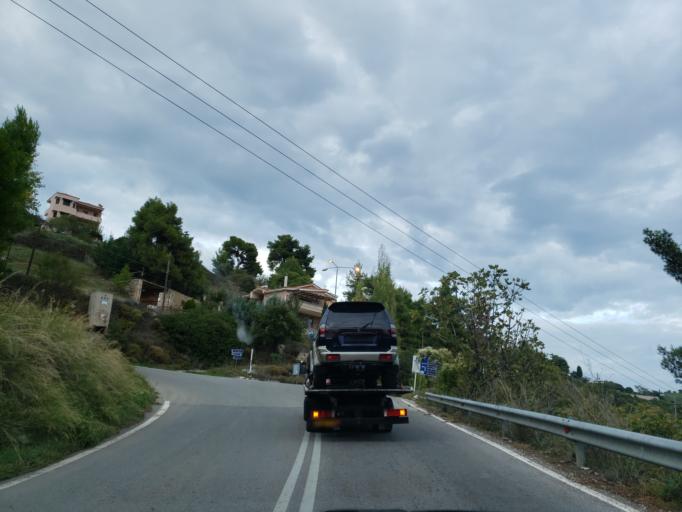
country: GR
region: Attica
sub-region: Nomarchia Anatolikis Attikis
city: Varnavas
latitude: 38.2193
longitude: 23.9207
